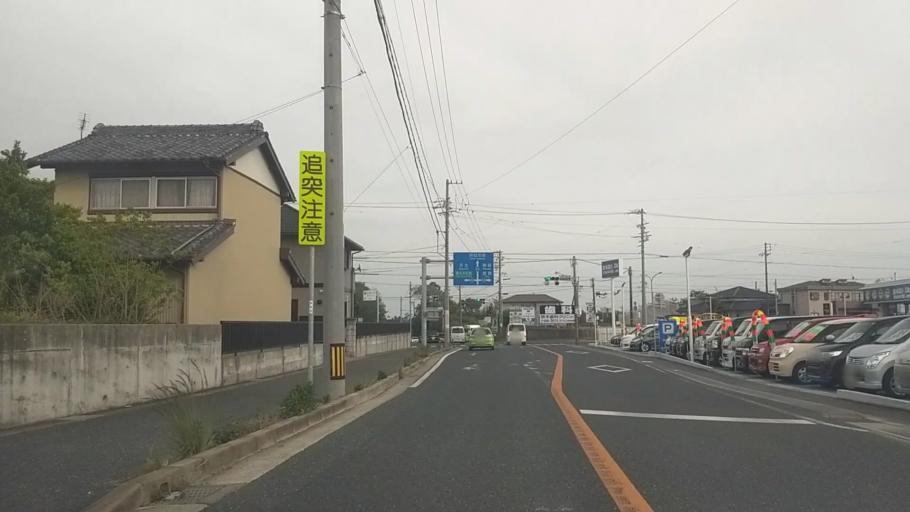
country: JP
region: Shizuoka
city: Hamamatsu
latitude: 34.7526
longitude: 137.6720
